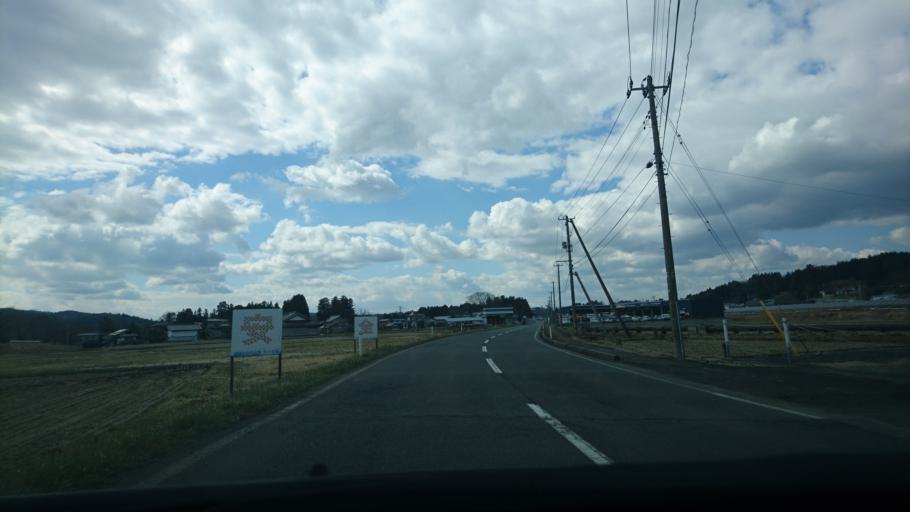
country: JP
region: Iwate
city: Hanamaki
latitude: 39.3776
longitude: 141.2404
